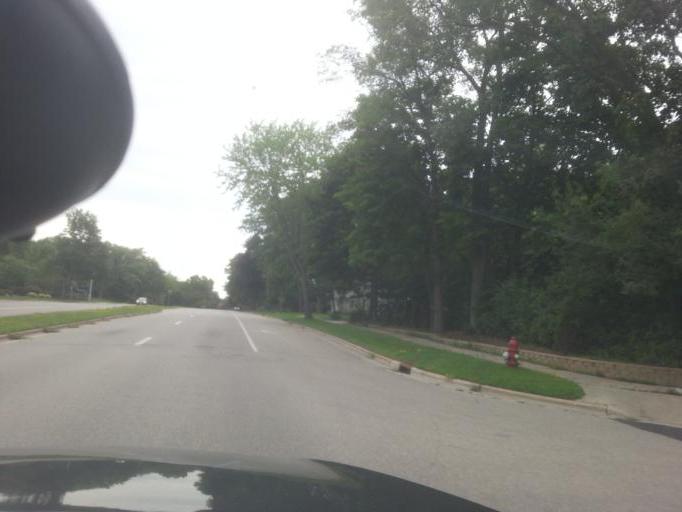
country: US
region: Wisconsin
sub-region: Dane County
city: Shorewood Hills
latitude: 43.0689
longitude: -89.4683
